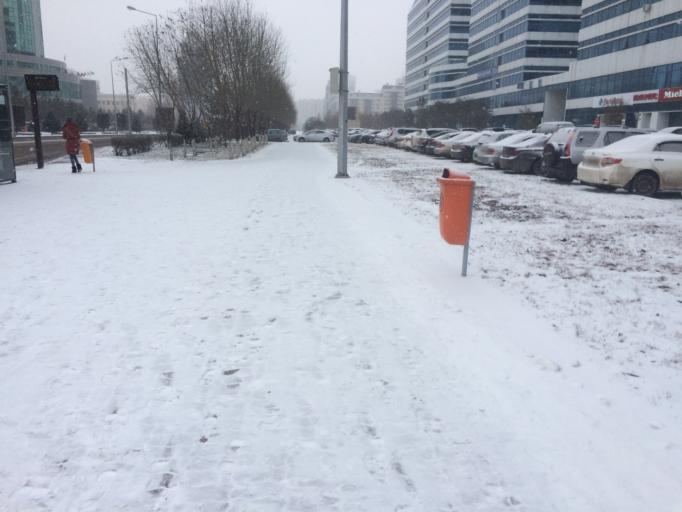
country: KZ
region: Astana Qalasy
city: Astana
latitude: 51.1312
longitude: 71.4262
